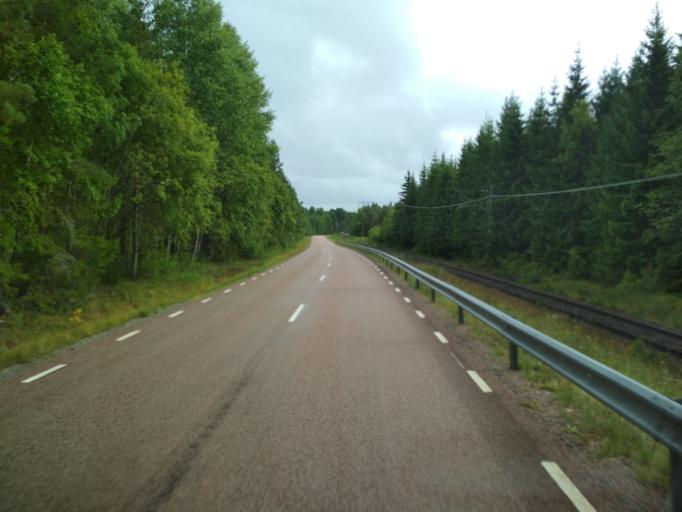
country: SE
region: Vaestmanland
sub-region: Surahammars Kommun
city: Ramnas
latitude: 59.8055
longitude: 16.1684
